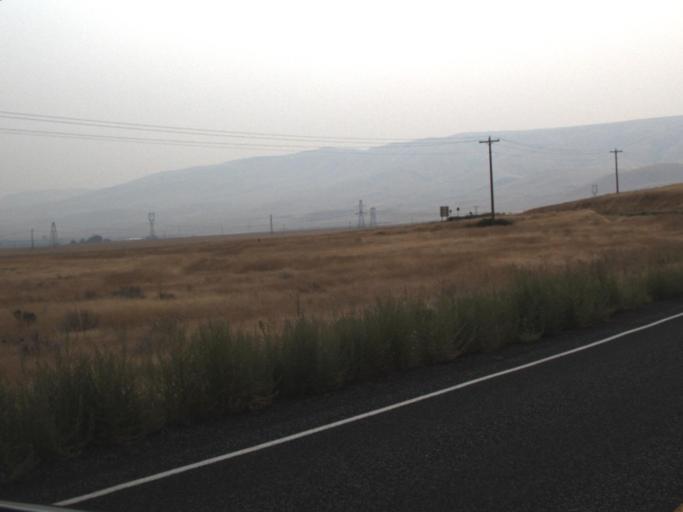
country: US
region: Washington
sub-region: Grant County
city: Desert Aire
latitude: 46.5245
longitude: -119.8744
